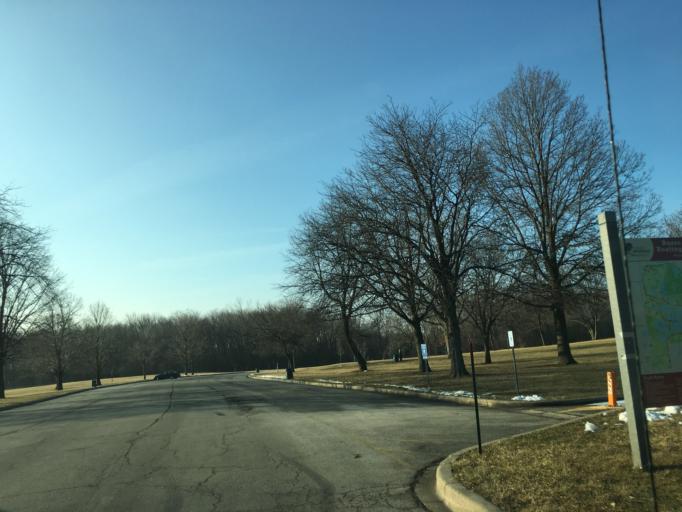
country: US
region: Illinois
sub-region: Cook County
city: Hoffman Estates
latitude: 42.0335
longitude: -88.0279
